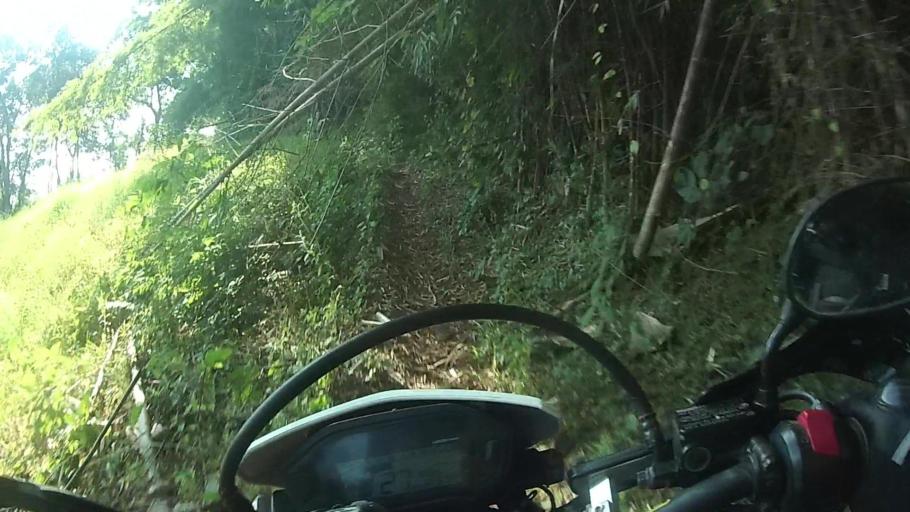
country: TH
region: Chiang Mai
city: Phrao
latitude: 19.4139
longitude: 99.2973
